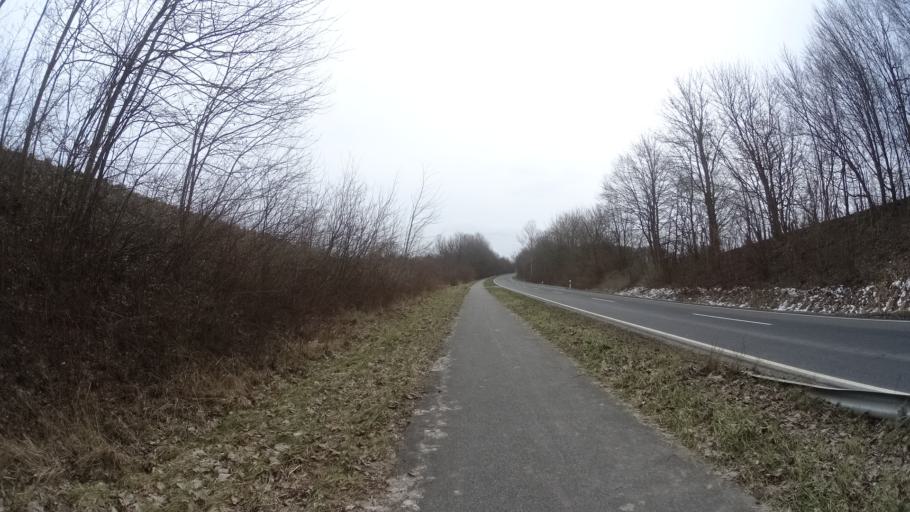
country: DE
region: Schleswig-Holstein
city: Hohenfelde
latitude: 54.3727
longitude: 10.5026
